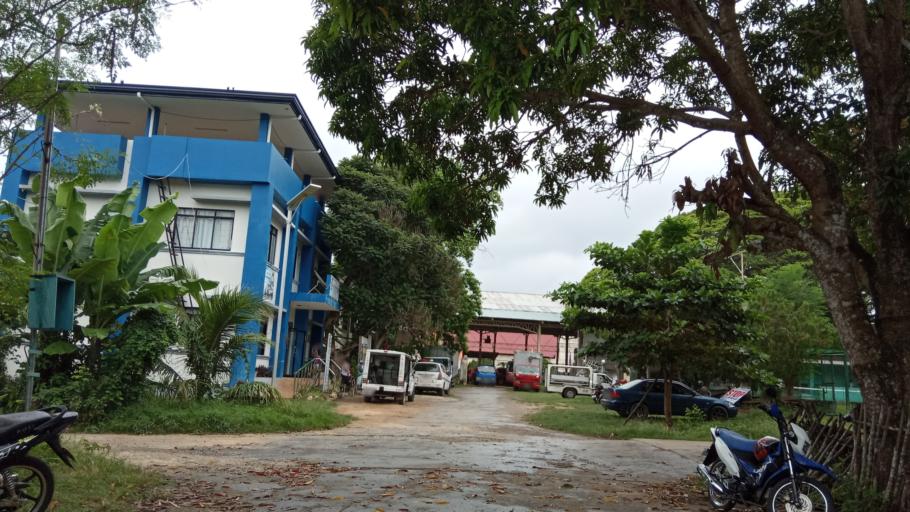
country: PH
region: Central Visayas
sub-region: Province of Siquijor
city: Lazi
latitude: 9.1291
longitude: 123.6331
